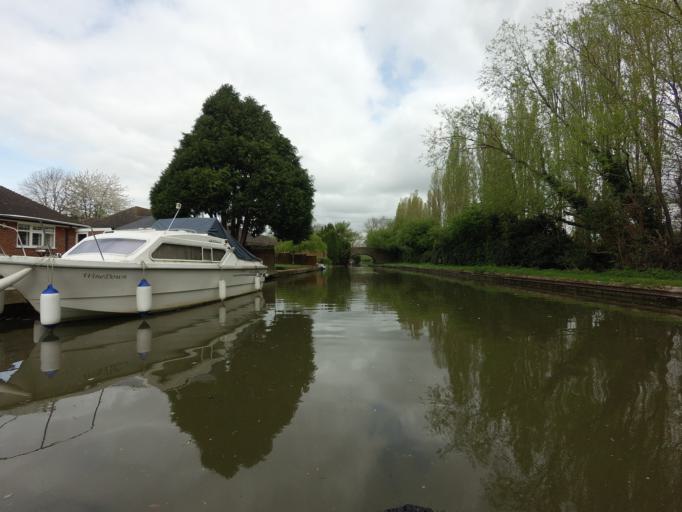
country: GB
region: England
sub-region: Milton Keynes
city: Water Eaton
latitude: 51.9874
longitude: -0.7175
